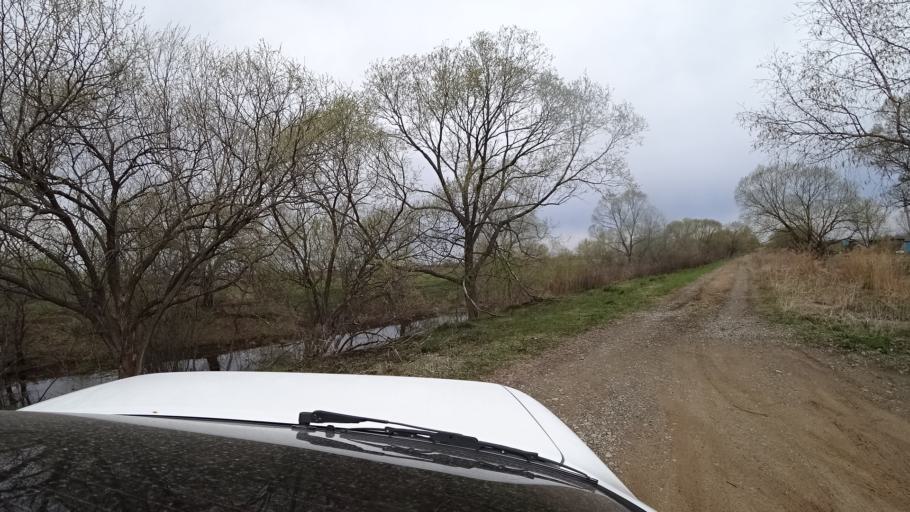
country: RU
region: Primorskiy
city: Dal'nerechensk
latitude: 45.9762
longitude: 133.7517
